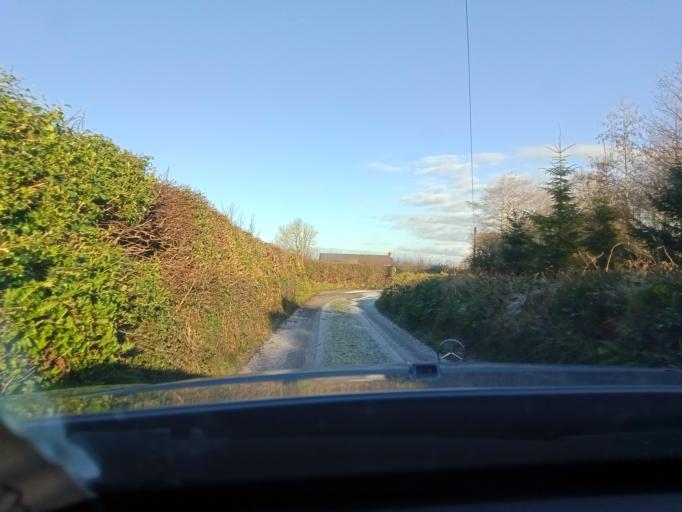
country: IE
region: Leinster
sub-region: Kilkenny
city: Graiguenamanagh
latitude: 52.5604
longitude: -6.9433
